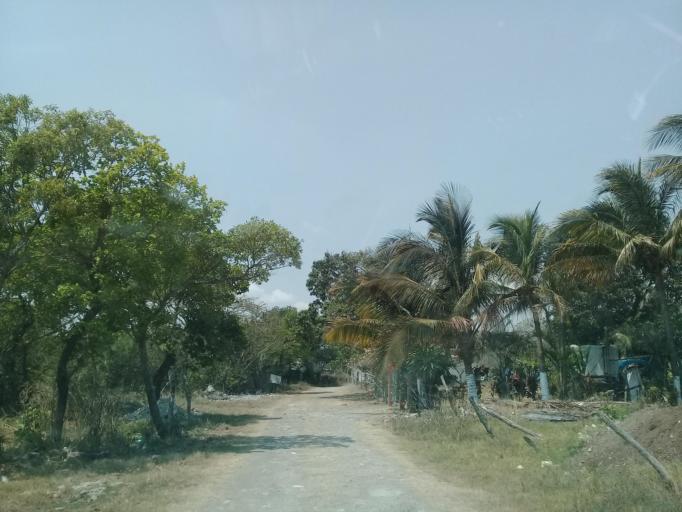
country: MX
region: Veracruz
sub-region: Veracruz
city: Hacienda Sotavento
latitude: 19.1345
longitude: -96.1824
